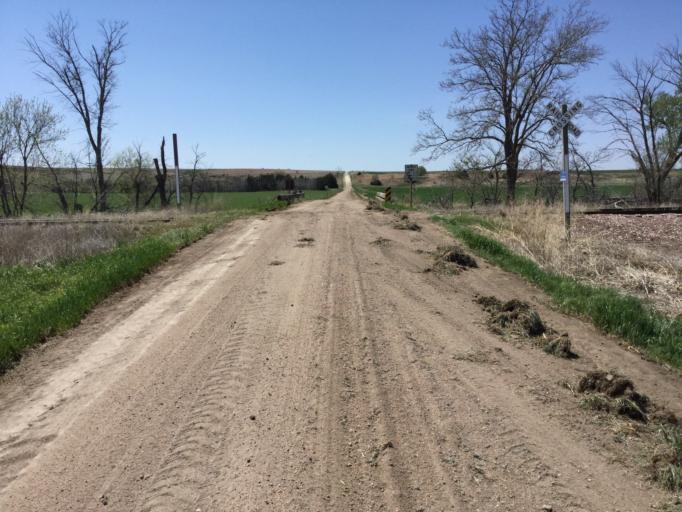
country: US
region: Kansas
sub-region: Decatur County
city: Oberlin
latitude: 39.9138
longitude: -100.7217
